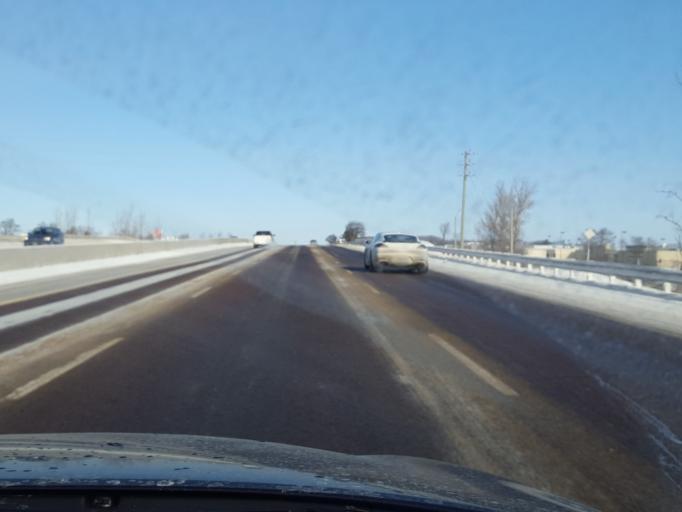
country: CA
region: Ontario
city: Innisfil
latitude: 44.3341
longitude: -79.6843
